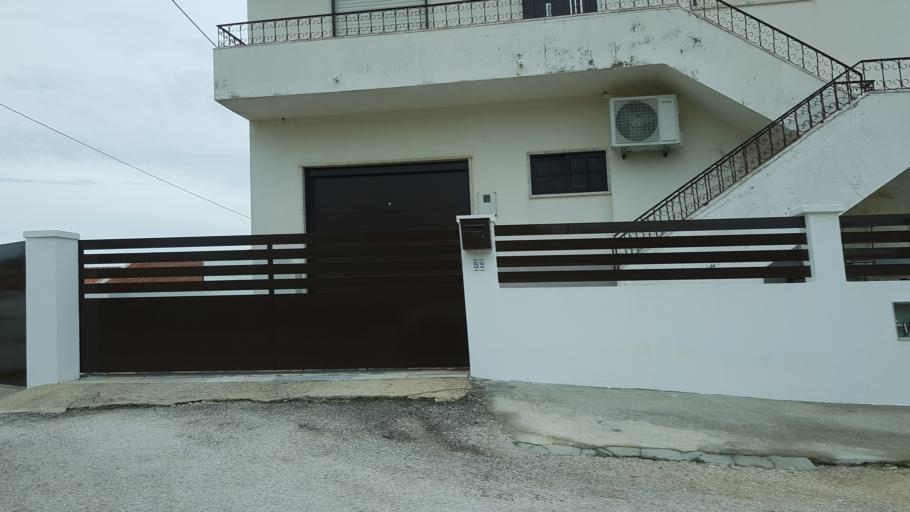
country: PT
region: Lisbon
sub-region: Alenquer
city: Alenquer
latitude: 39.0383
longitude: -8.9986
